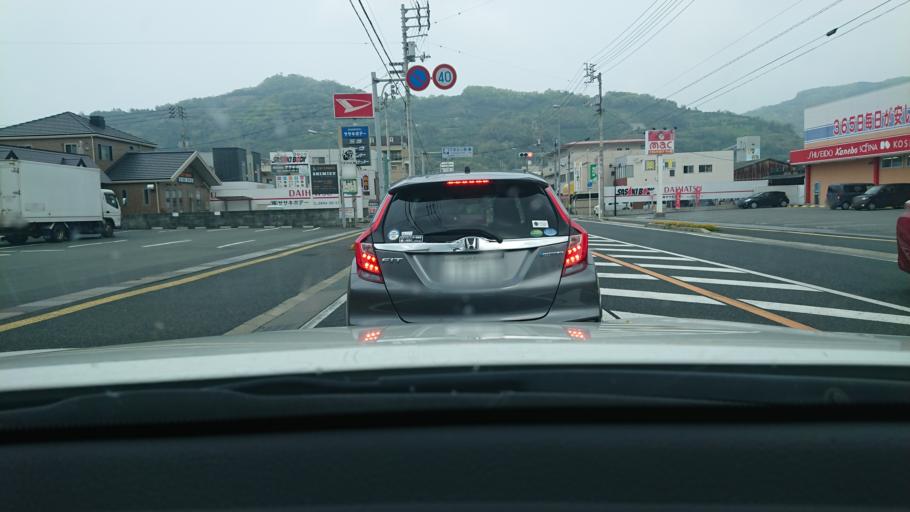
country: JP
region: Ehime
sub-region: Nishiuwa-gun
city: Ikata-cho
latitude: 33.4839
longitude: 132.4028
